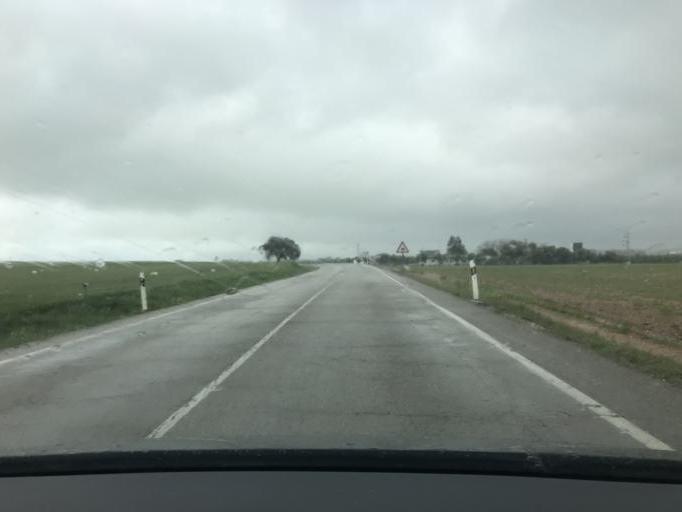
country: ES
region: Andalusia
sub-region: Provincia de Sevilla
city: La Luisiana
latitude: 37.4445
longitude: -5.2444
